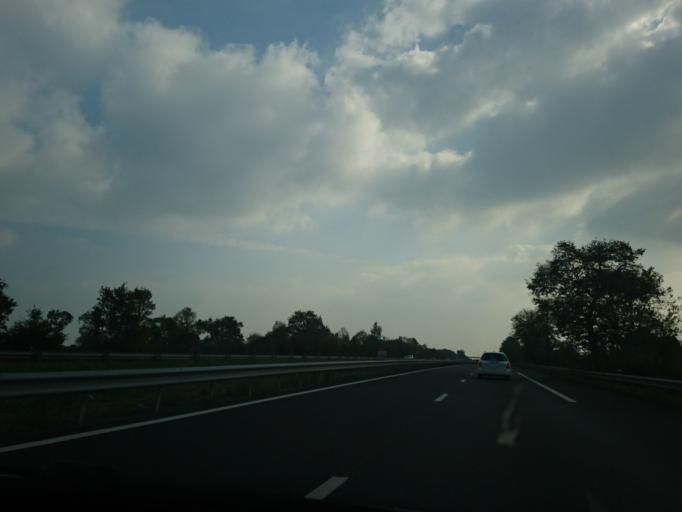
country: FR
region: Pays de la Loire
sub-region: Departement de la Loire-Atlantique
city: La Grigonnais
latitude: 47.4975
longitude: -1.6384
